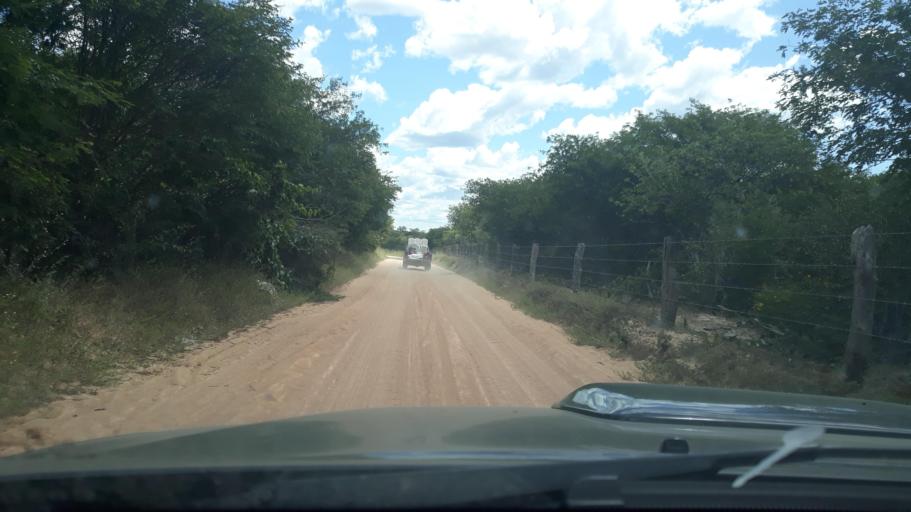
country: BR
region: Bahia
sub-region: Riacho De Santana
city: Riacho de Santana
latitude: -13.9080
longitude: -42.9339
